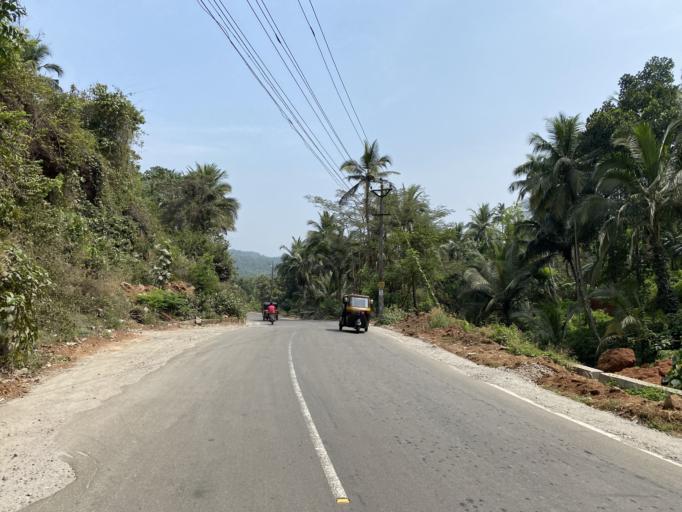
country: IN
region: Kerala
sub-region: Malappuram
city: Malappuram
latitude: 11.0537
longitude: 75.9982
